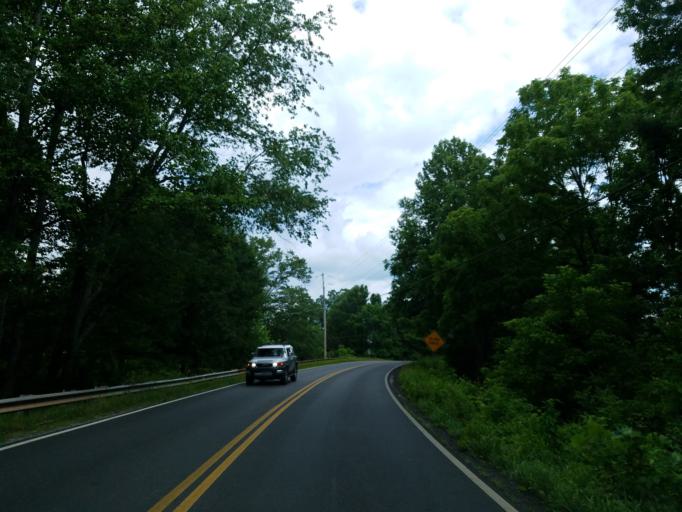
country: US
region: Georgia
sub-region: Fannin County
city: Blue Ridge
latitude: 34.8633
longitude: -84.3042
